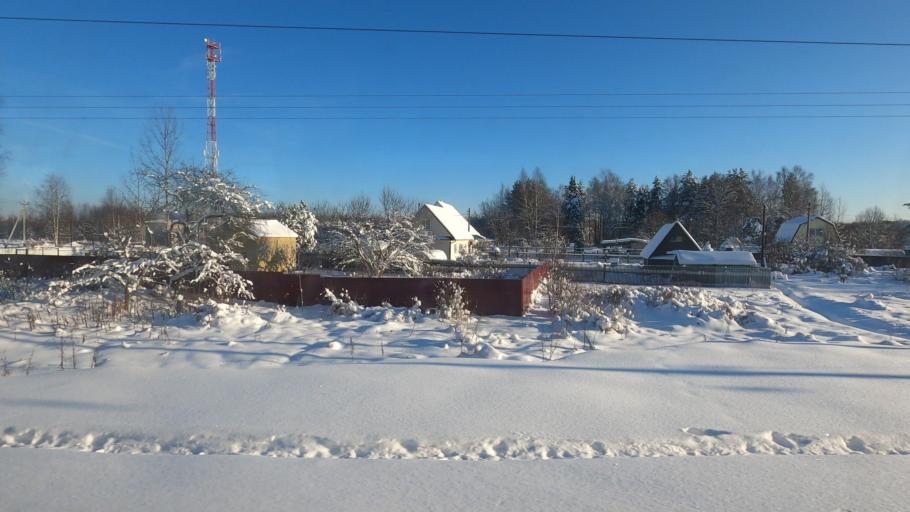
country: RU
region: Moskovskaya
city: Novo-Nikol'skoye
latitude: 56.6437
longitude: 37.5625
